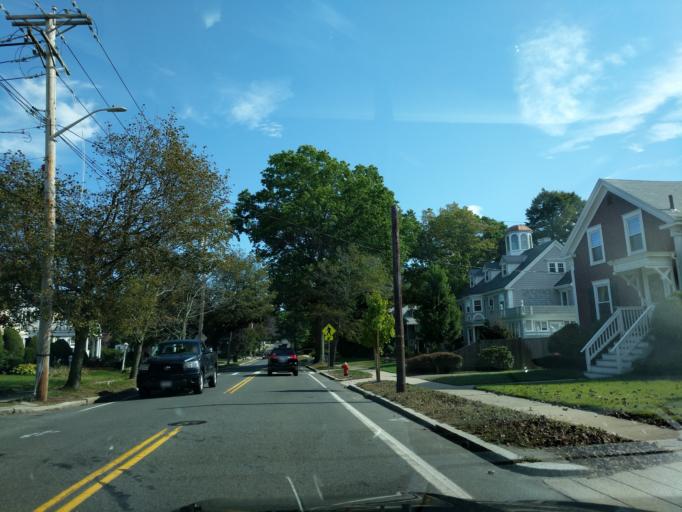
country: US
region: Massachusetts
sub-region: Middlesex County
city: Melrose
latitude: 42.4580
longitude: -71.0551
